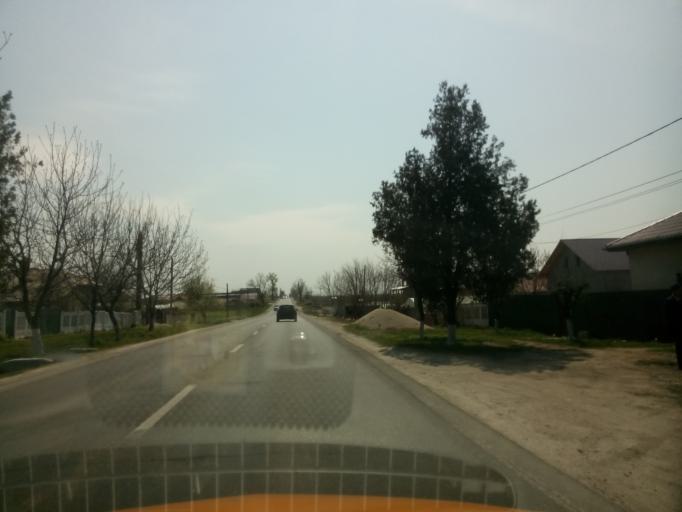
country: RO
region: Calarasi
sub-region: Comuna Frumusani
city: Frumusani
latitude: 44.2775
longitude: 26.3360
